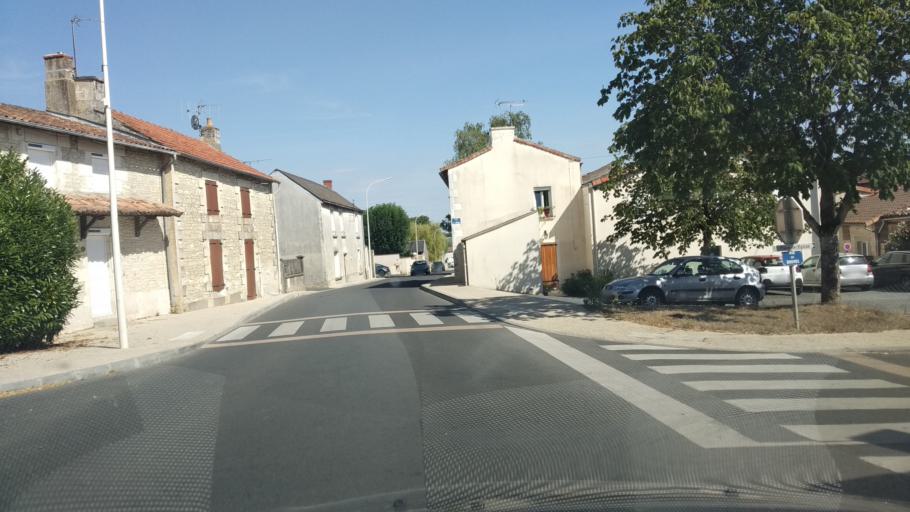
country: FR
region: Poitou-Charentes
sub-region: Departement de la Vienne
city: Cisse
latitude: 46.6472
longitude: 0.2268
